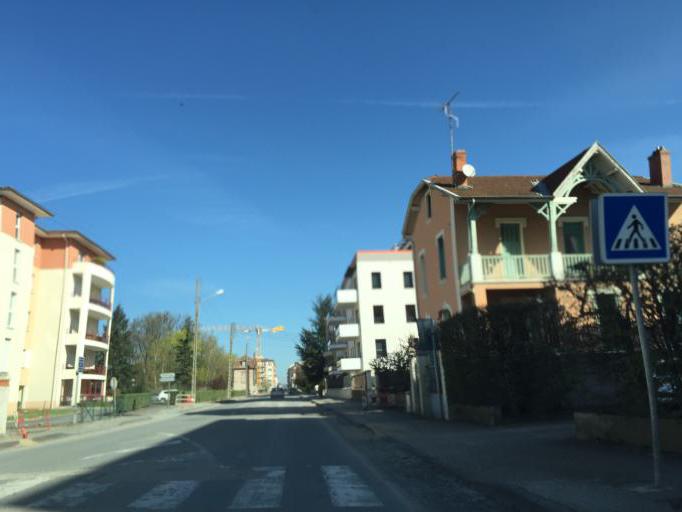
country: FR
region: Rhone-Alpes
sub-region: Departement de la Loire
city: Feurs
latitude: 45.7388
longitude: 4.2245
